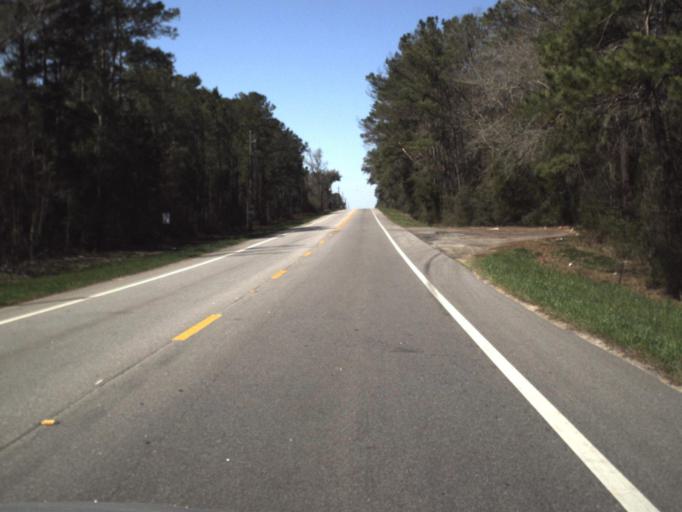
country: US
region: Florida
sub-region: Jackson County
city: Marianna
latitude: 30.7945
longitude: -85.2682
